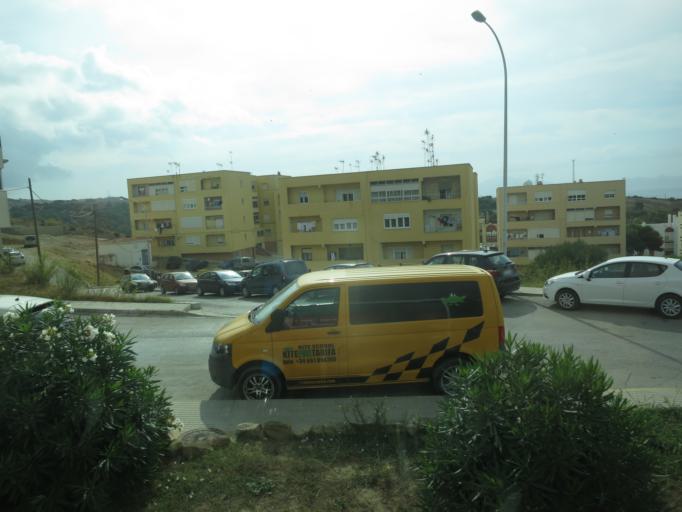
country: ES
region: Andalusia
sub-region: Provincia de Cadiz
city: Tarifa
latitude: 36.0159
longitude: -5.6019
